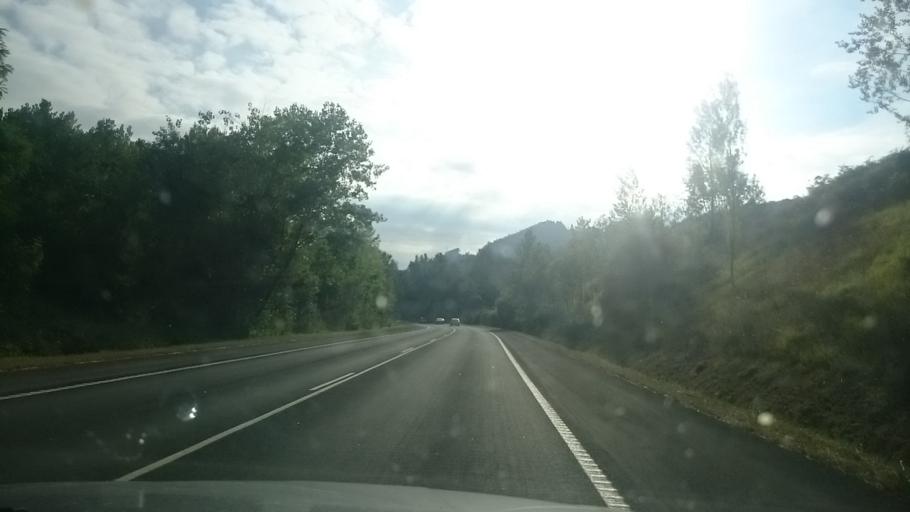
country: ES
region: Asturias
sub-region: Province of Asturias
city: Norena
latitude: 43.3341
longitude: -5.7641
